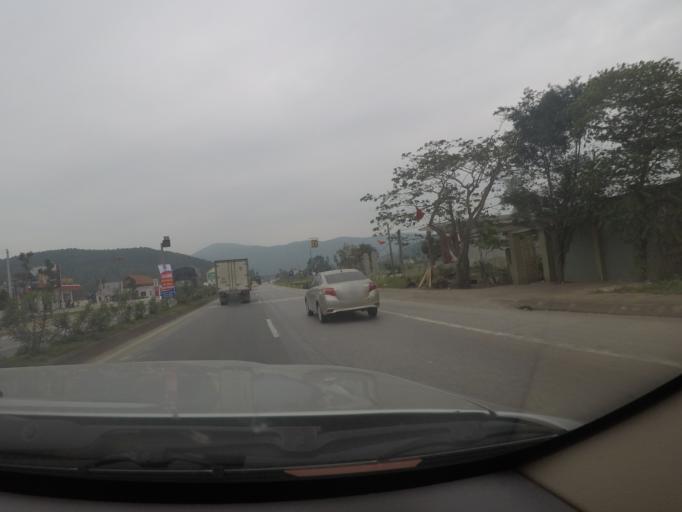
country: VN
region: Nghe An
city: Dien Chau
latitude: 18.9031
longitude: 105.6039
